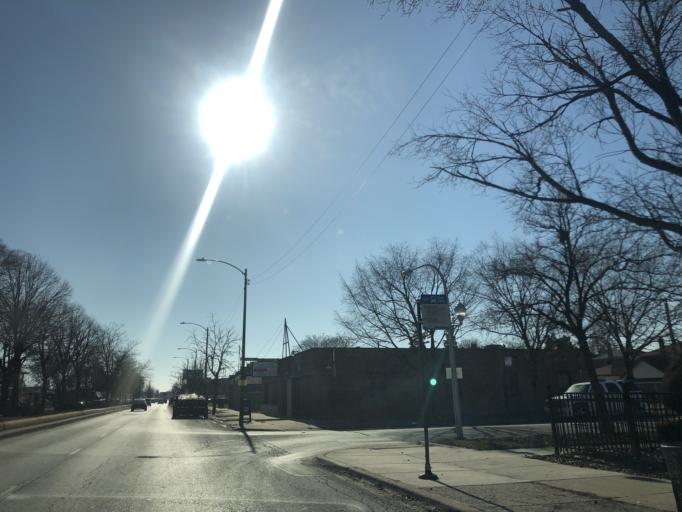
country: US
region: Illinois
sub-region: Cook County
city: Evergreen Park
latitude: 41.7196
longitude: -87.6432
